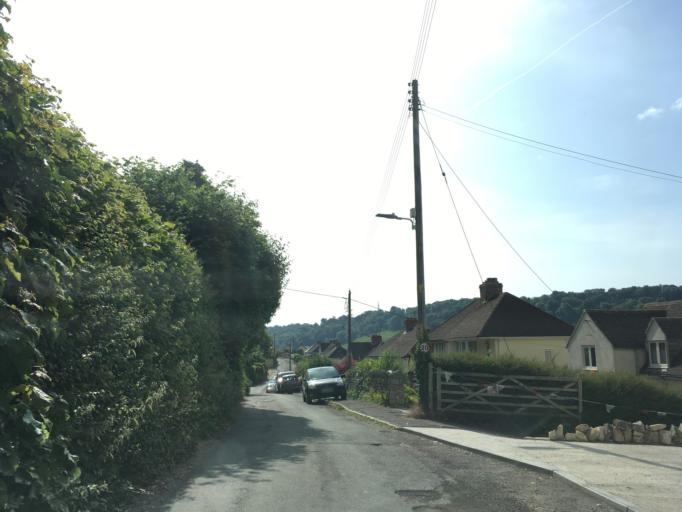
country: GB
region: England
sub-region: Gloucestershire
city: Brimscombe
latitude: 51.7205
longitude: -2.1882
